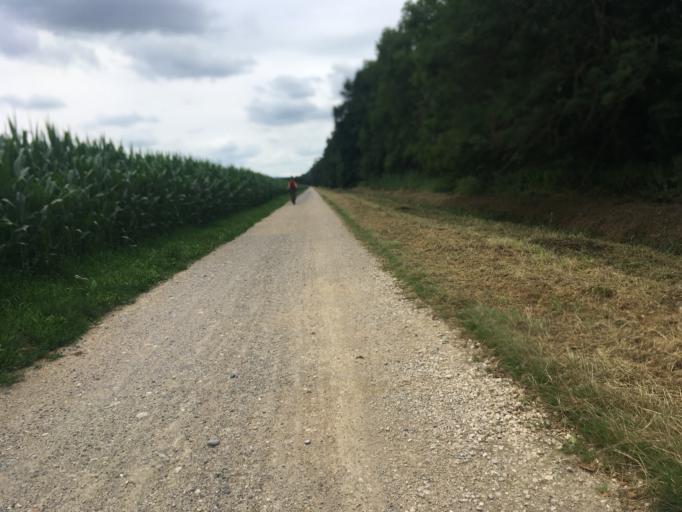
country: CH
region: Vaud
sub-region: Broye-Vully District
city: Avenches
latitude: 46.8979
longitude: 7.0346
